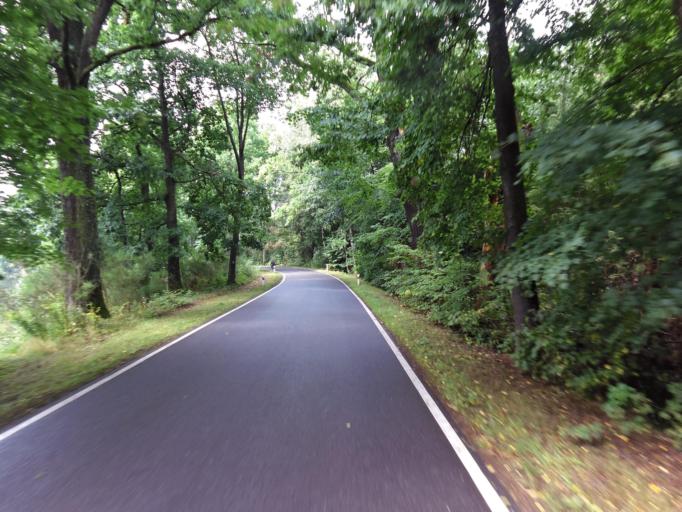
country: CZ
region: Jihocesky
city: Chlum u Trebone
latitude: 48.9470
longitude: 14.9181
